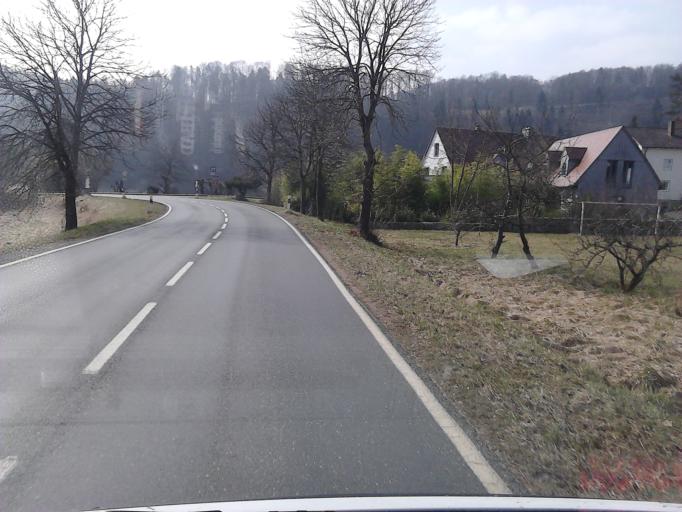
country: DE
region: Bavaria
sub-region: Upper Franconia
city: Gossweinstein
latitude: 49.7808
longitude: 11.3341
